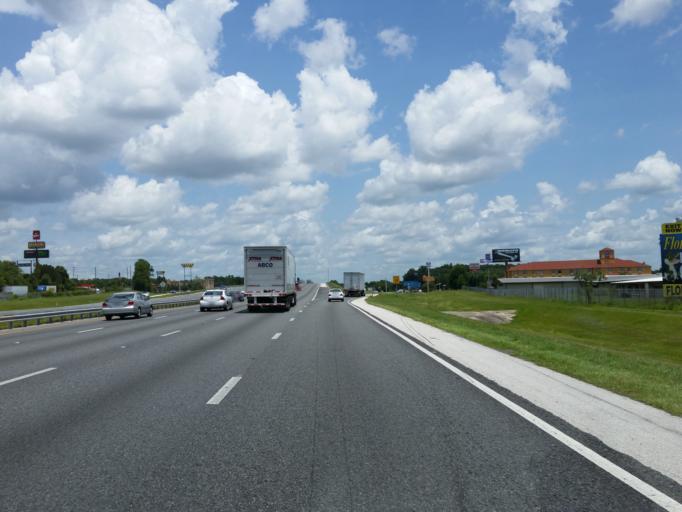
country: US
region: Florida
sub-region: Marion County
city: Belleview
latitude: 29.0212
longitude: -82.1560
